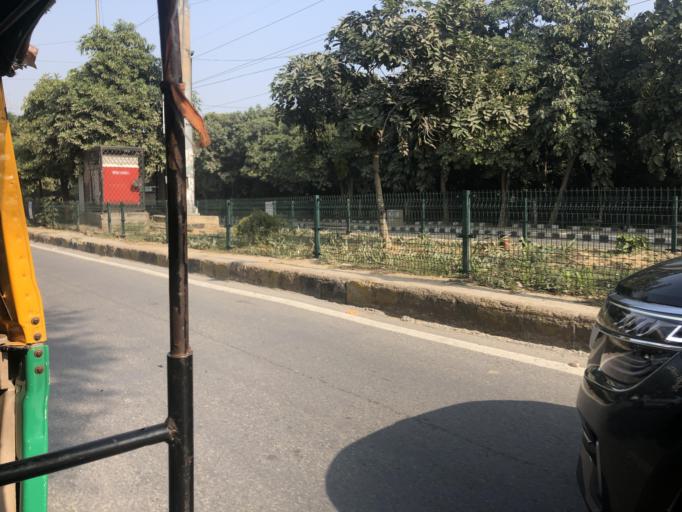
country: IN
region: Haryana
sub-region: Gurgaon
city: Gurgaon
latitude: 28.4309
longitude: 77.0912
